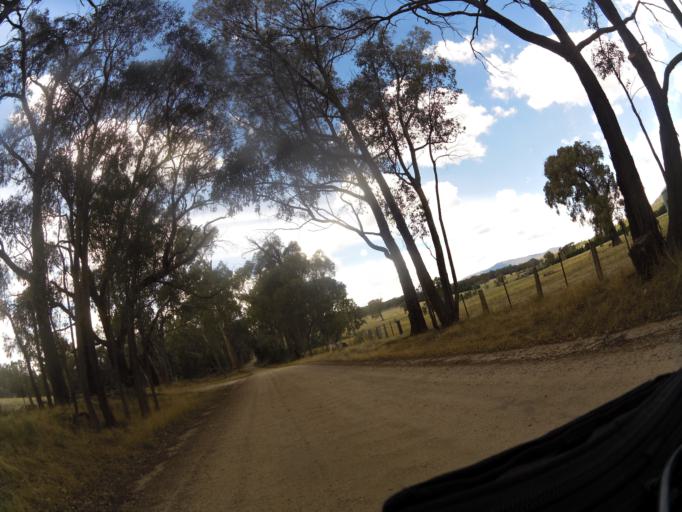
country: AU
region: Victoria
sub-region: Benalla
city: Benalla
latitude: -36.7820
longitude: 145.9949
